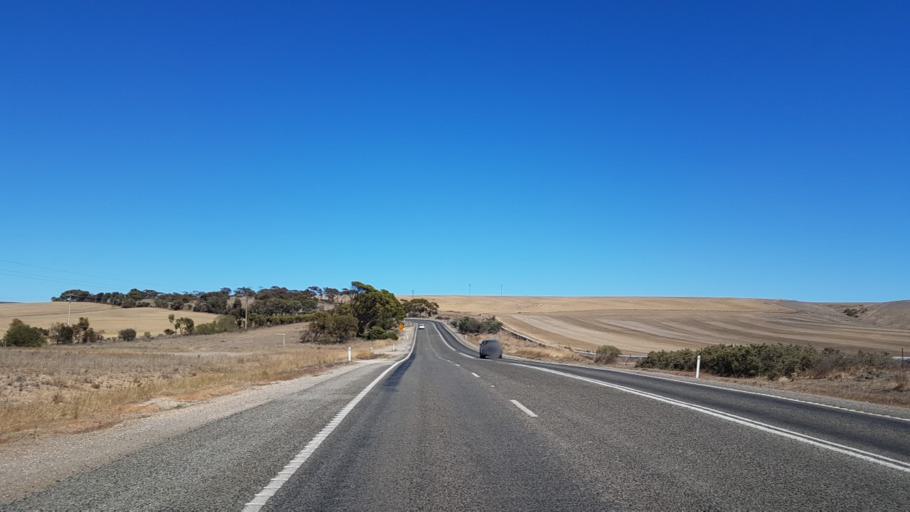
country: AU
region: South Australia
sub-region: Copper Coast
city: Kadina
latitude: -34.0651
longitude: 138.0567
